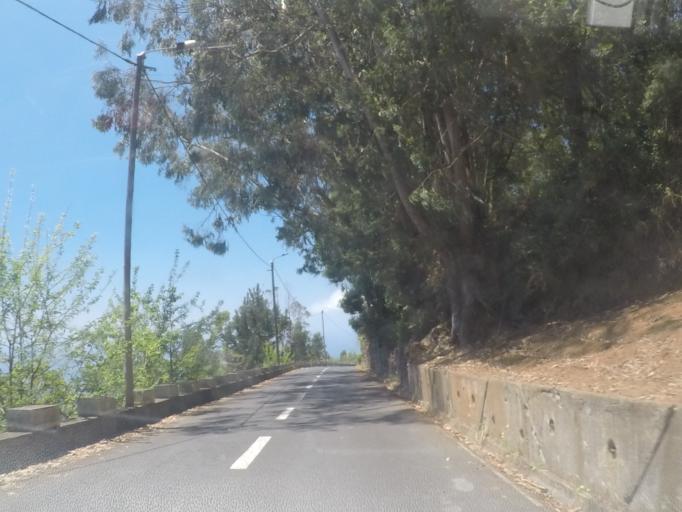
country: PT
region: Madeira
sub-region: Camara de Lobos
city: Curral das Freiras
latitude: 32.6867
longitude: -16.9857
